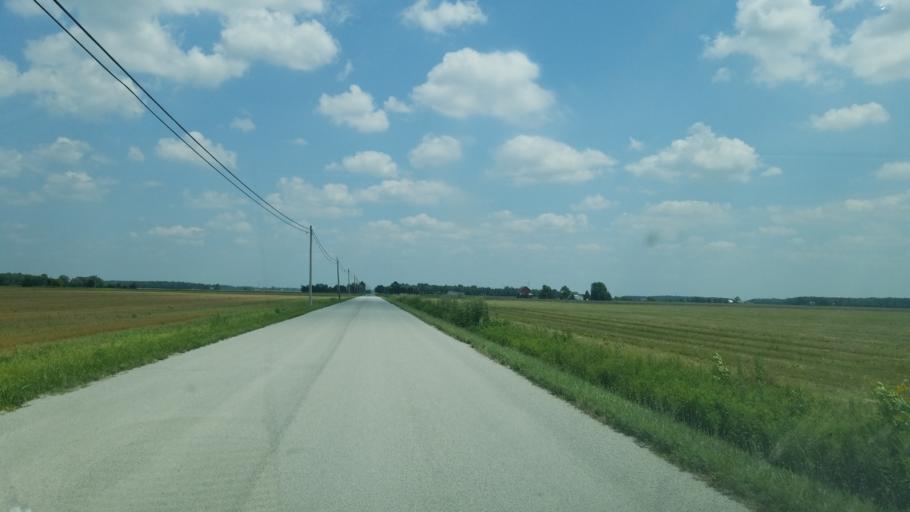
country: US
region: Ohio
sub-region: Wood County
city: North Baltimore
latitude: 41.2400
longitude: -83.6006
